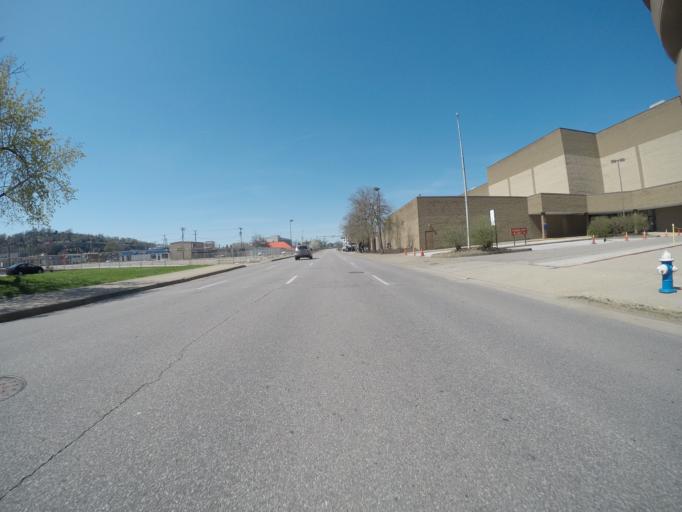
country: US
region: West Virginia
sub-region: Kanawha County
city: Charleston
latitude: 38.3537
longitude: -81.6396
